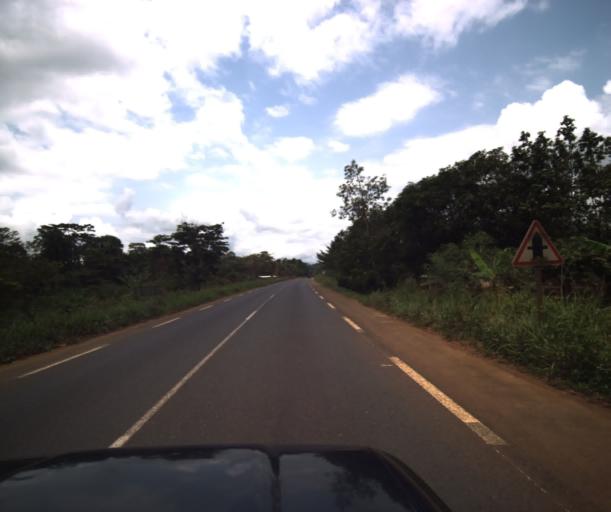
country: CM
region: Centre
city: Eseka
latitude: 3.8720
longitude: 10.8971
